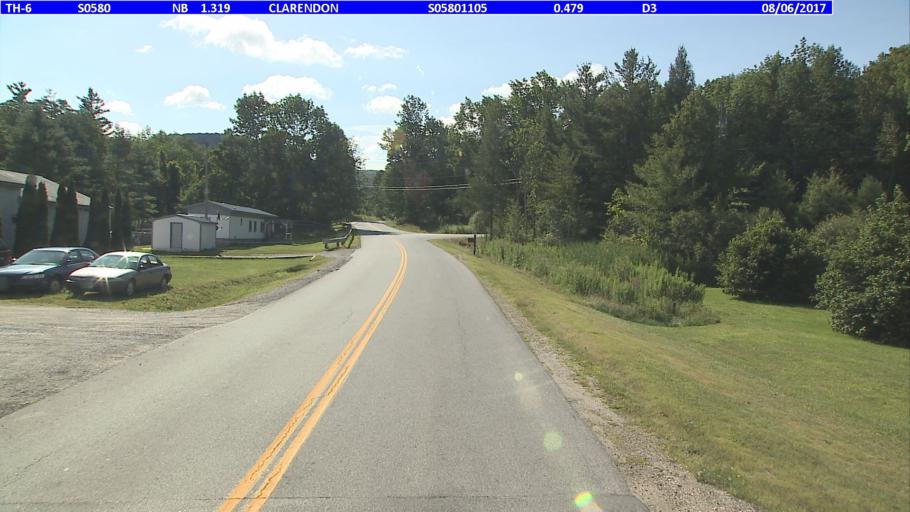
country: US
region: Vermont
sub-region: Rutland County
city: Rutland
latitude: 43.5682
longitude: -72.9484
